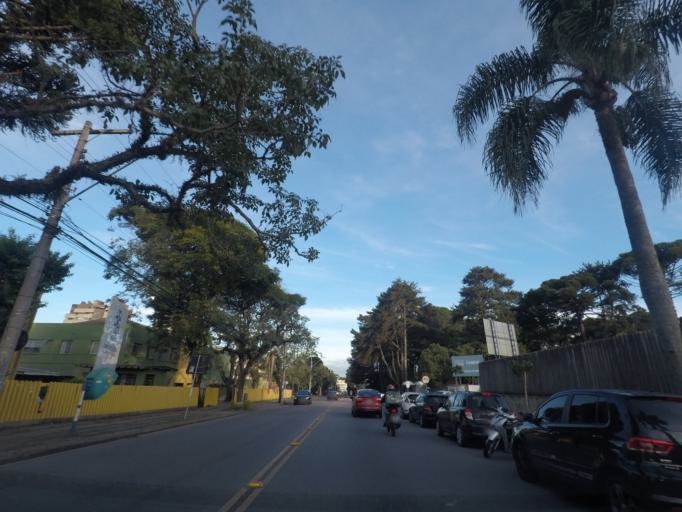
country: BR
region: Parana
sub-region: Curitiba
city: Curitiba
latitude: -25.4097
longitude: -49.2490
